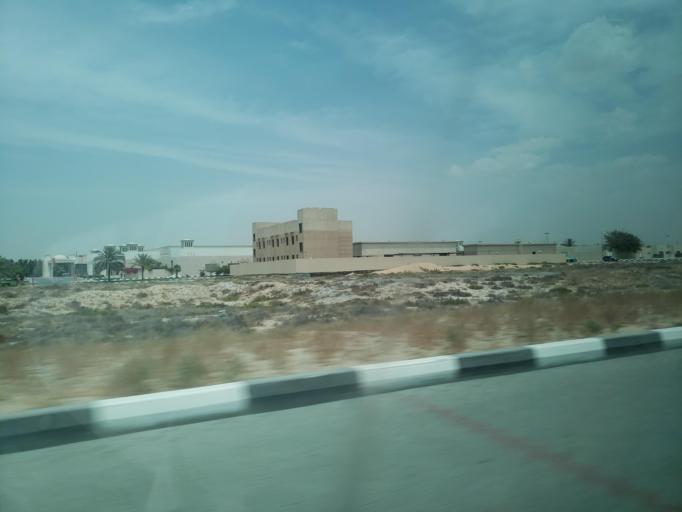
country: AE
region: Ash Shariqah
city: Sharjah
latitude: 25.3153
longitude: 55.5125
